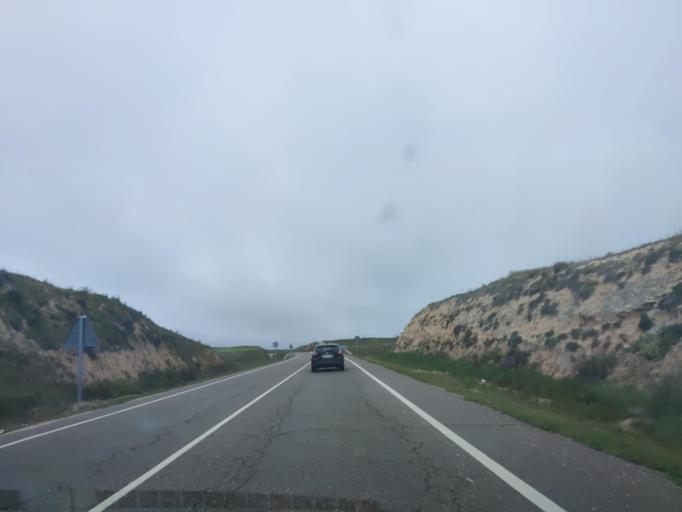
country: ES
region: Castille-La Mancha
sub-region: Province of Toledo
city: Bargas
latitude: 39.9462
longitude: -4.0231
